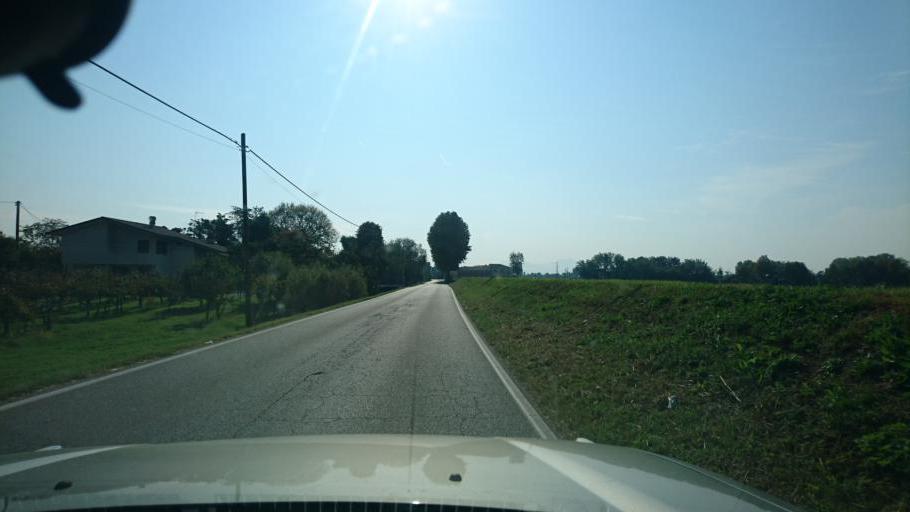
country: IT
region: Veneto
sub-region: Provincia di Vicenza
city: Longare
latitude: 45.4841
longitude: 11.6122
